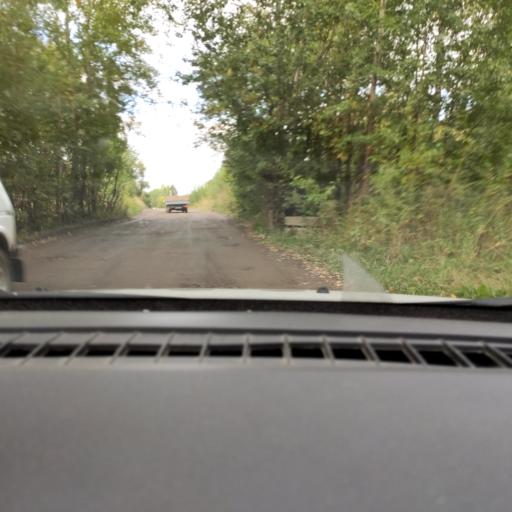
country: RU
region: Perm
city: Perm
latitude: 58.1116
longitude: 56.3871
